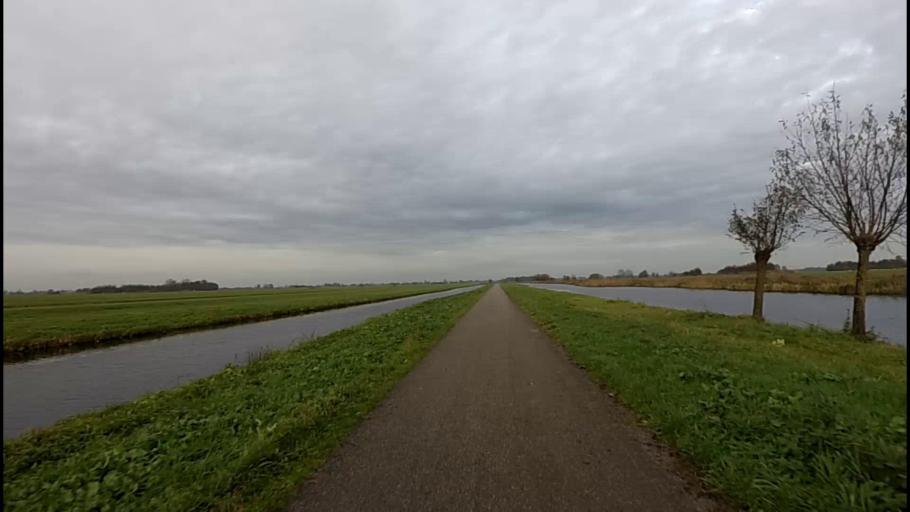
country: NL
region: South Holland
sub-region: Gemeente Vlist
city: Haastrecht
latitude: 51.9408
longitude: 4.7379
